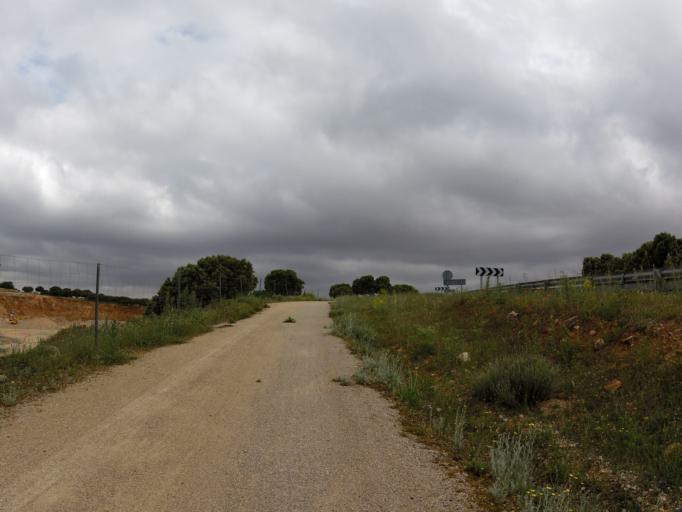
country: ES
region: Castille-La Mancha
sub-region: Provincia de Albacete
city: Robledo
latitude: 38.7344
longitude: -2.4670
